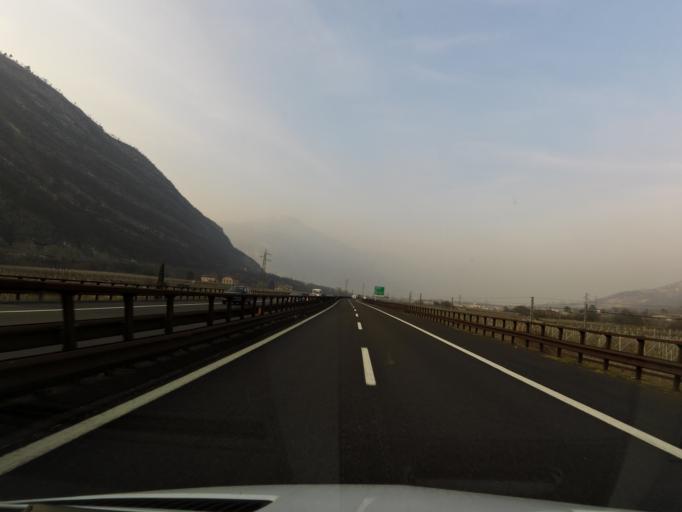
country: IT
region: Trentino-Alto Adige
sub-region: Provincia di Trento
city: Marco
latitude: 45.8269
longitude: 11.0038
